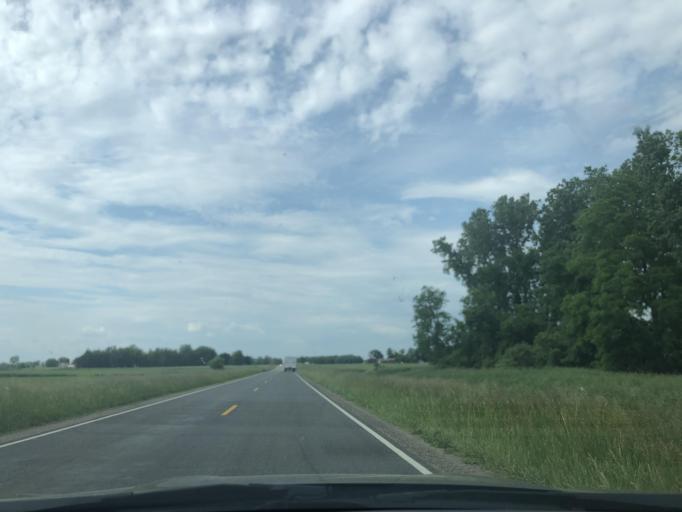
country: US
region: Michigan
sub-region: Clinton County
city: Saint Johns
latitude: 42.9848
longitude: -84.4838
